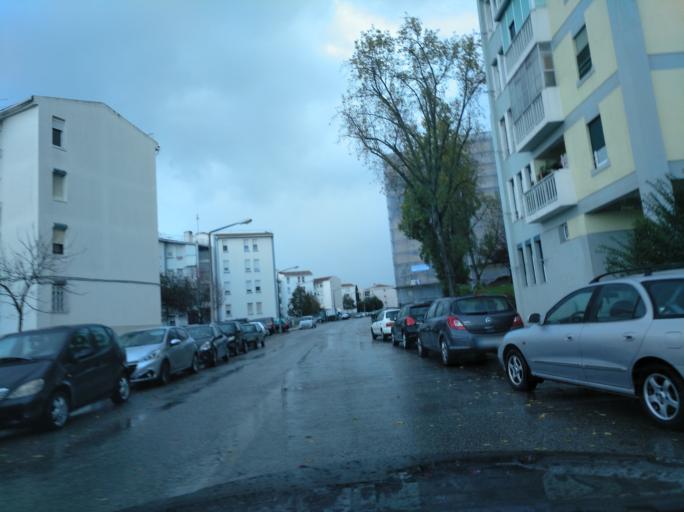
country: PT
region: Lisbon
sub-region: Loures
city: Moscavide
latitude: 38.7614
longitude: -9.1067
